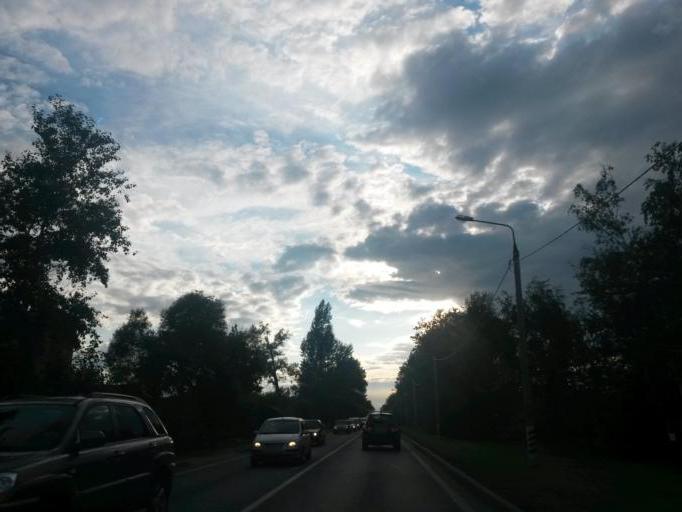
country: RU
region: Moskovskaya
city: Vostryakovo
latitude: 55.3937
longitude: 37.8001
